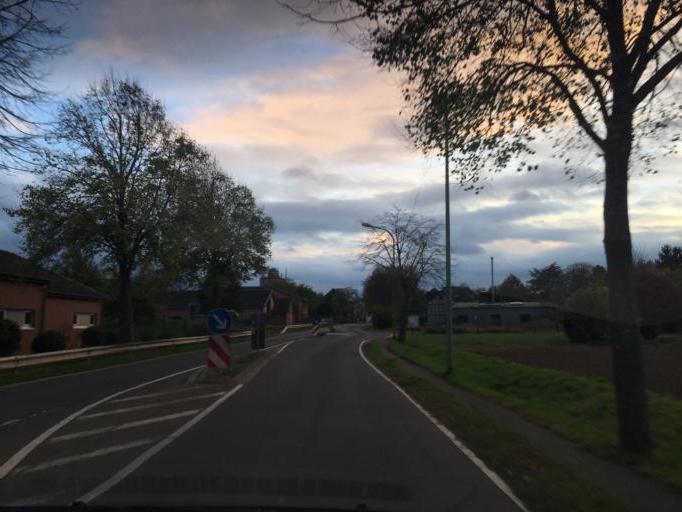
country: DE
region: North Rhine-Westphalia
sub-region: Regierungsbezirk Koln
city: Vettweiss
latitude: 50.7444
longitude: 6.6046
